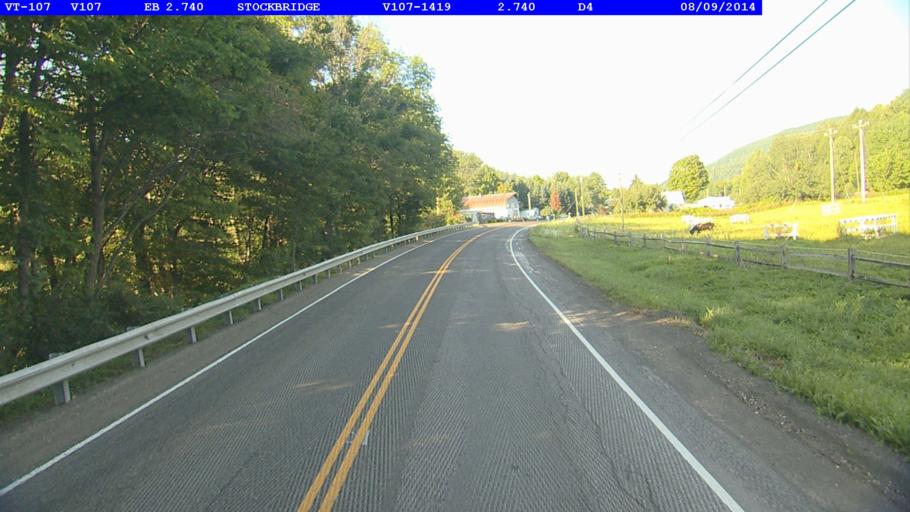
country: US
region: Vermont
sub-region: Orange County
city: Randolph
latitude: 43.7620
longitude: -72.7209
